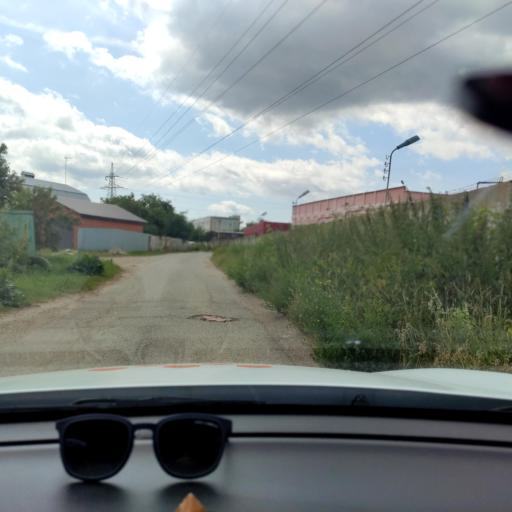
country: RU
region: Tatarstan
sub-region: Gorod Kazan'
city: Kazan
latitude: 55.8218
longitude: 49.1978
